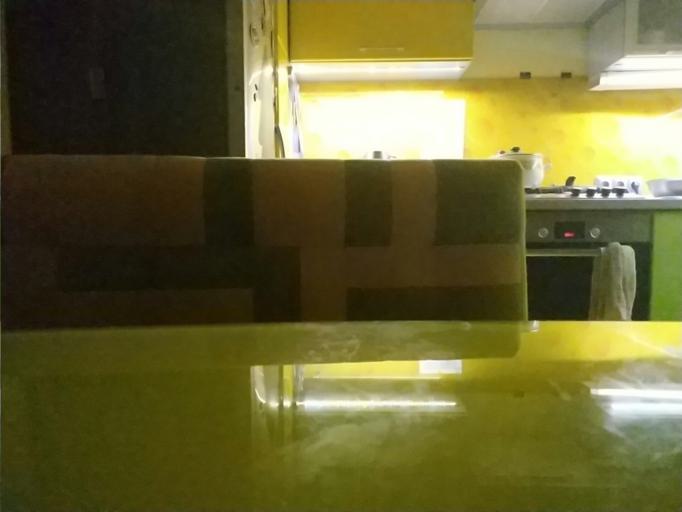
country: RU
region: Republic of Karelia
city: Kalevala
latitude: 65.2571
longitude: 30.7211
